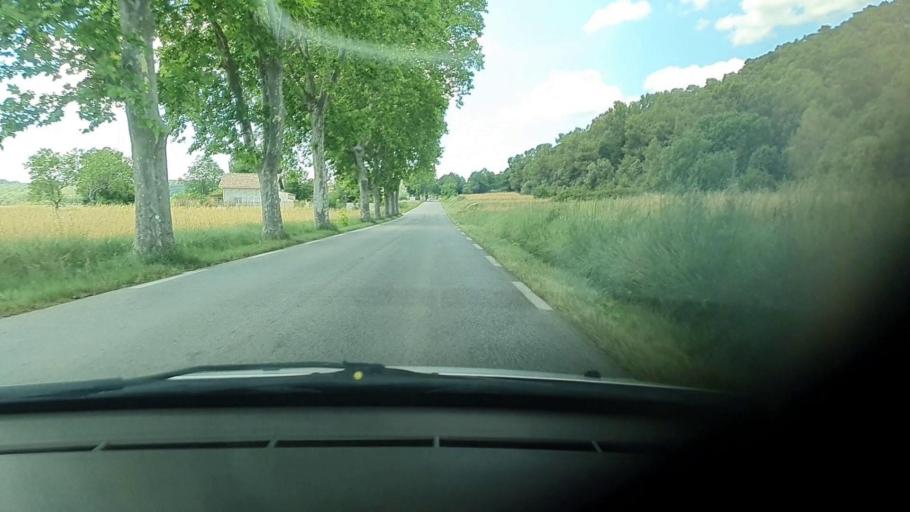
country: FR
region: Languedoc-Roussillon
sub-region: Departement du Gard
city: Montaren-et-Saint-Mediers
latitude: 44.0327
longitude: 4.3685
